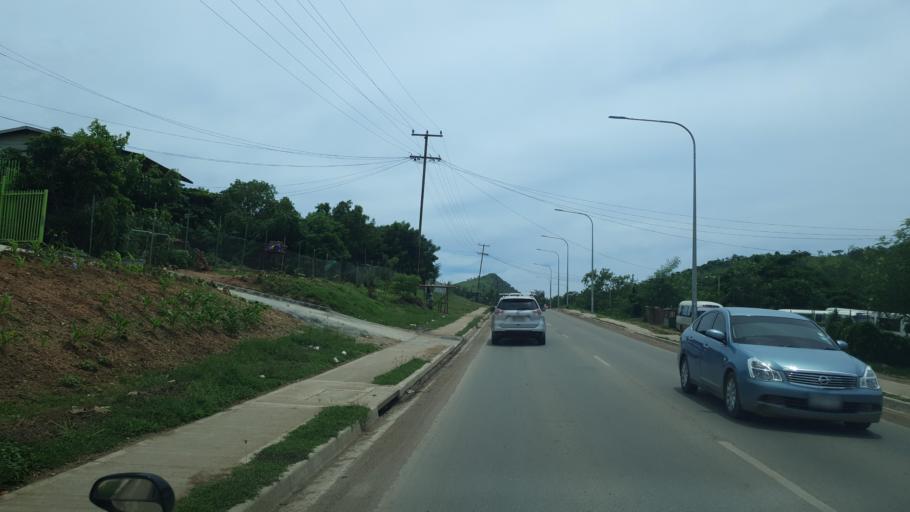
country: PG
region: National Capital
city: Port Moresby
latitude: -9.5109
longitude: 147.2421
